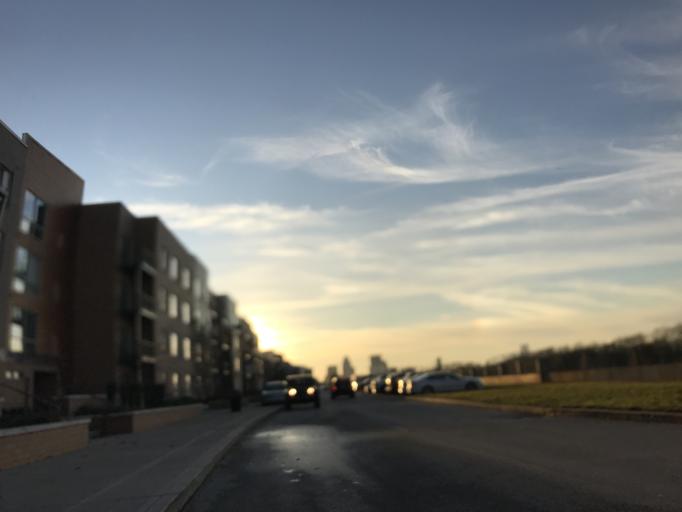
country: US
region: Indiana
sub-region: Clark County
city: Jeffersonville
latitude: 38.2657
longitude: -85.7242
